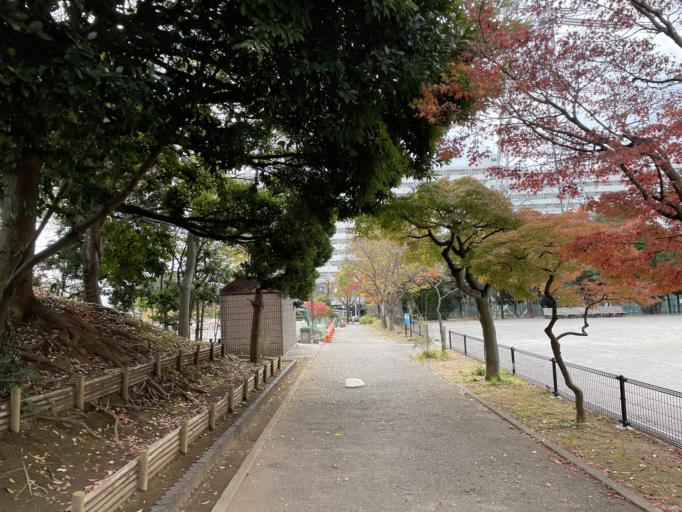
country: JP
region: Tokyo
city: Urayasu
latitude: 35.6484
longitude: 139.8825
